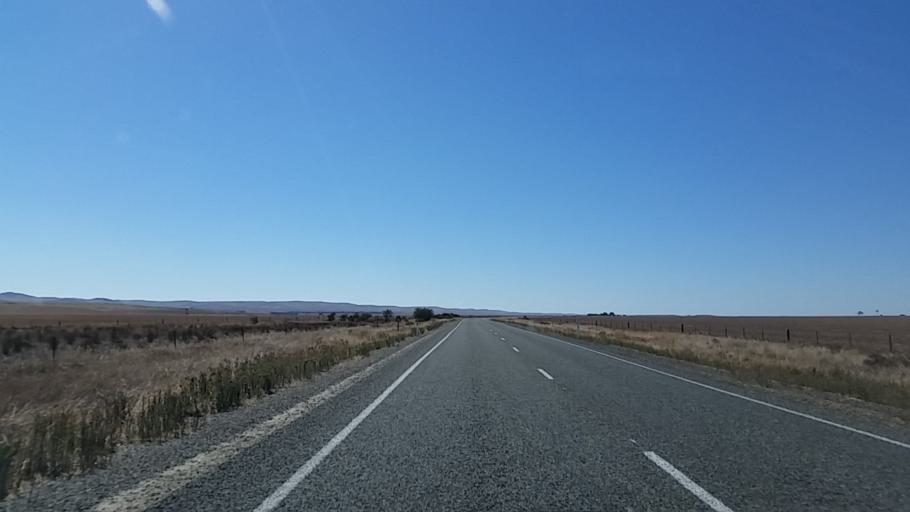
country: AU
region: South Australia
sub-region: Northern Areas
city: Jamestown
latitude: -33.2730
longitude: 138.8683
